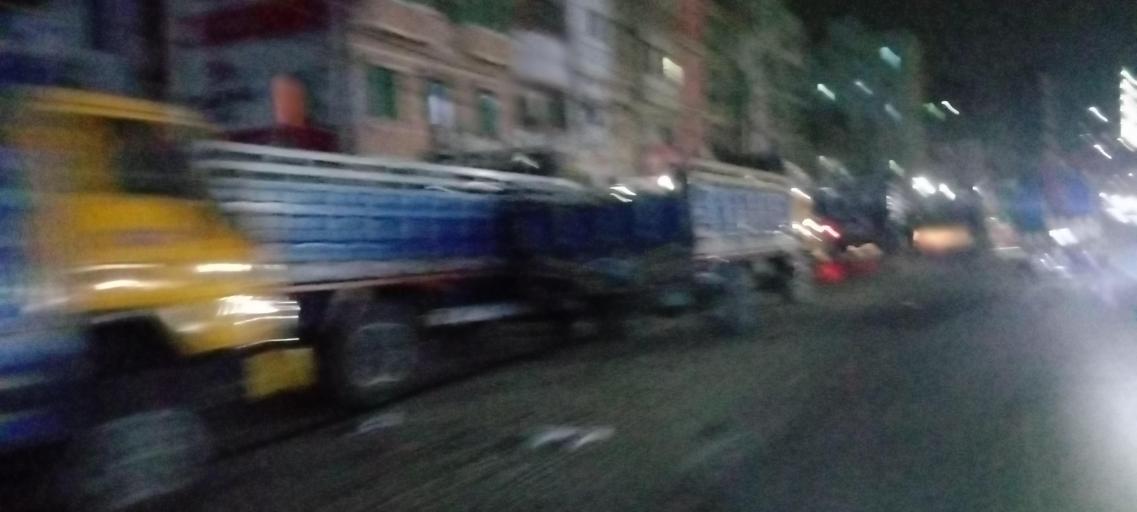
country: BD
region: Dhaka
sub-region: Dhaka
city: Dhaka
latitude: 23.7011
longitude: 90.3936
